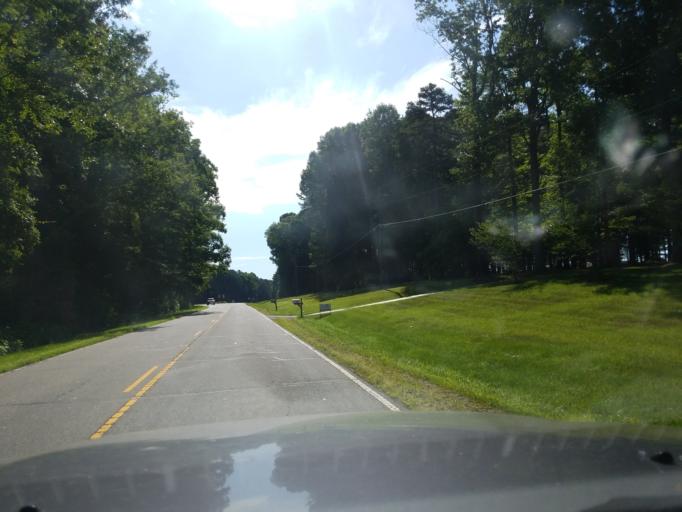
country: US
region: North Carolina
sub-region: Granville County
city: Oxford
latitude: 36.3154
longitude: -78.5171
